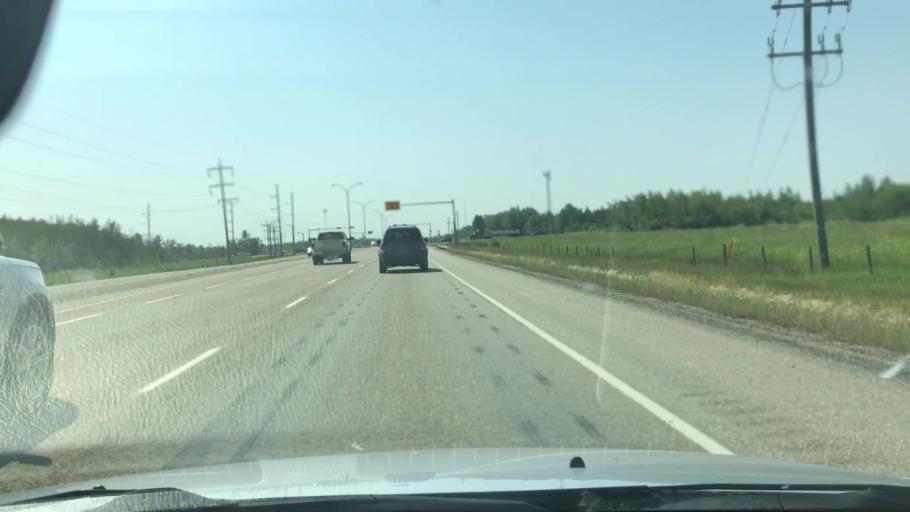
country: CA
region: Alberta
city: Devon
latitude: 53.4566
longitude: -113.7627
